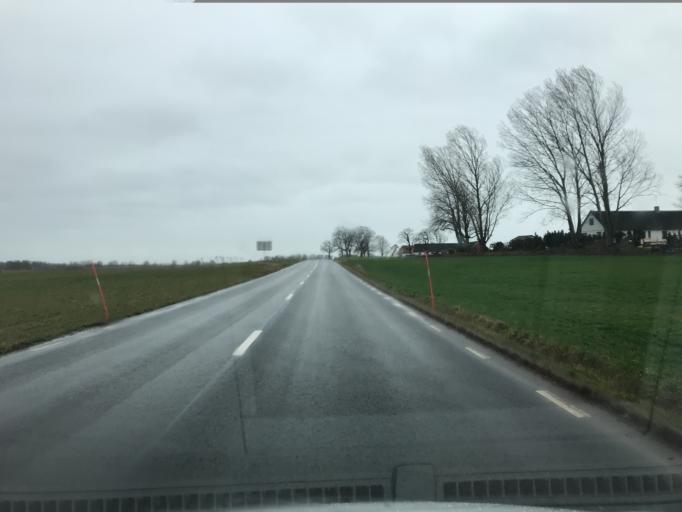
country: SE
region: Skane
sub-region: Bastads Kommun
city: Forslov
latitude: 56.3293
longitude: 12.8876
